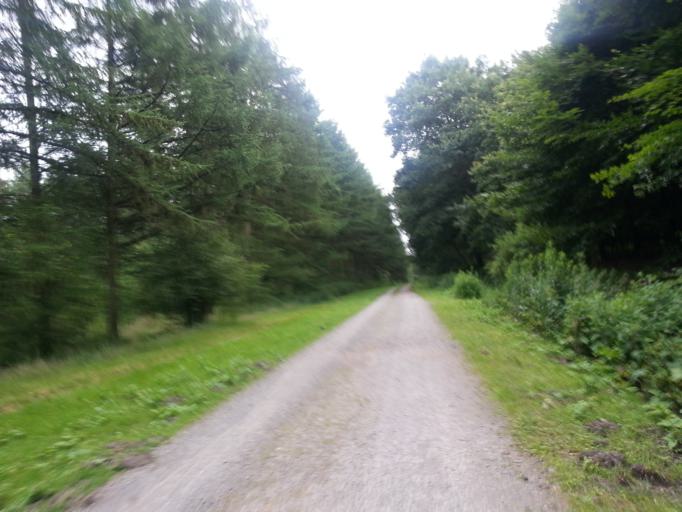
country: DE
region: North Rhine-Westphalia
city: Oer-Erkenschwick
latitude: 51.6833
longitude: 7.2222
